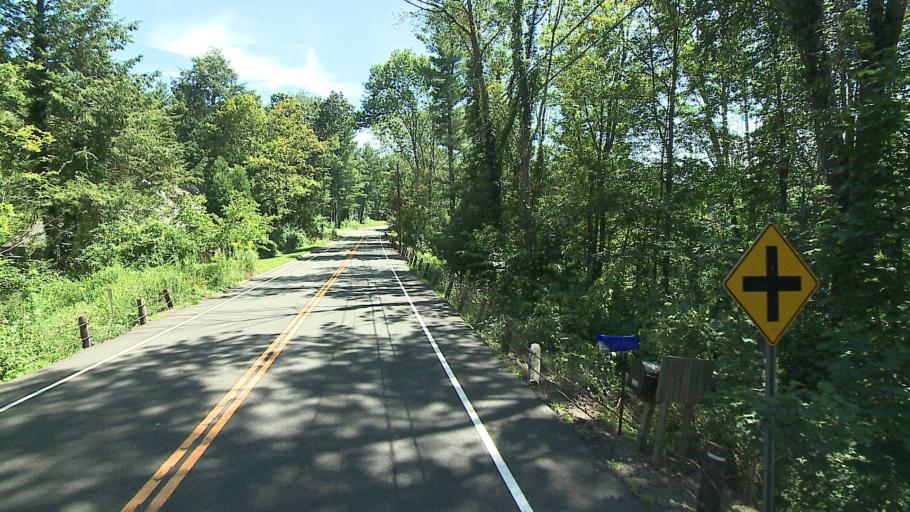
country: US
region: Connecticut
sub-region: Litchfield County
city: New Hartford Center
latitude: 41.9296
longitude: -72.9676
